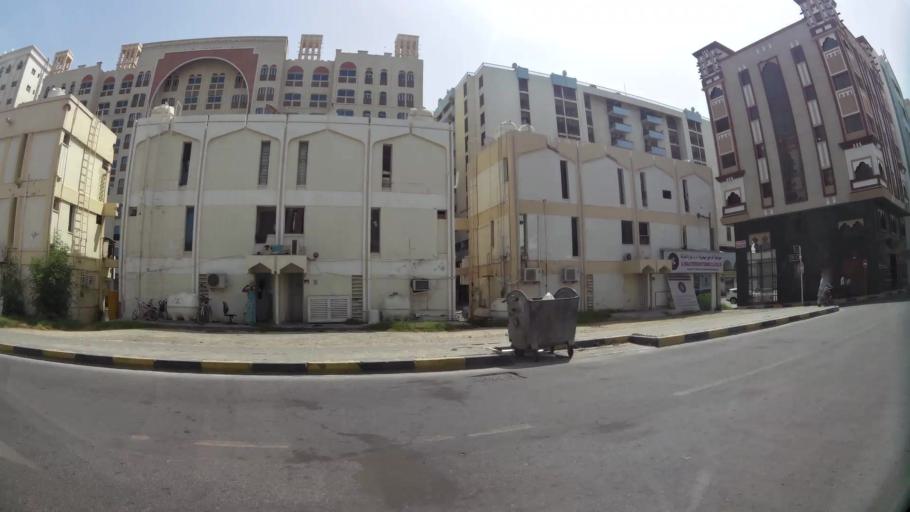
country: AE
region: Ash Shariqah
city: Sharjah
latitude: 25.3537
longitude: 55.3831
